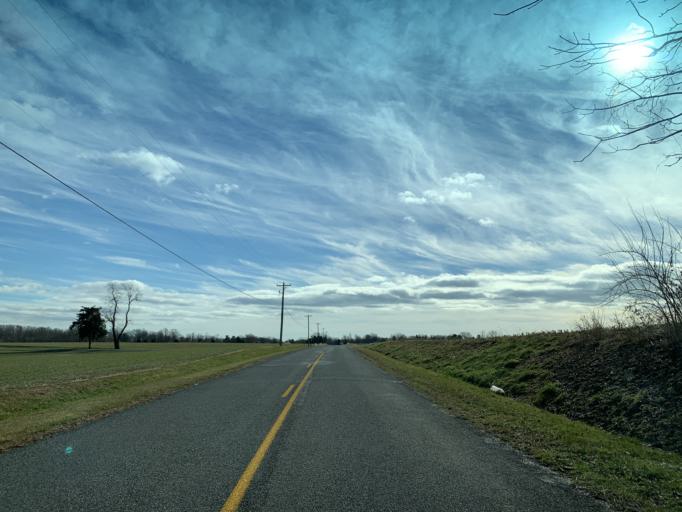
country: US
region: Maryland
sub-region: Kent County
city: Chestertown
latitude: 39.3361
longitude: -76.0472
